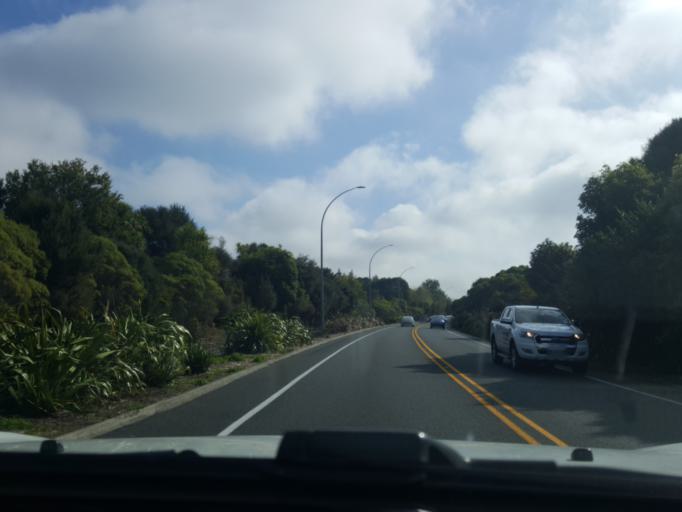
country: NZ
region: Waikato
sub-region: Hamilton City
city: Hamilton
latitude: -37.7436
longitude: 175.2692
